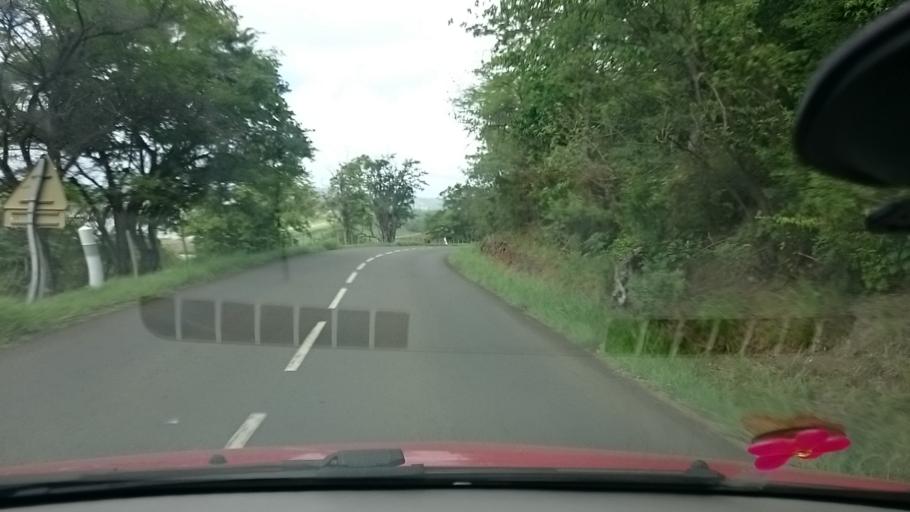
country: MQ
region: Martinique
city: Petite Riviere Salee
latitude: 14.7573
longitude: -60.9334
